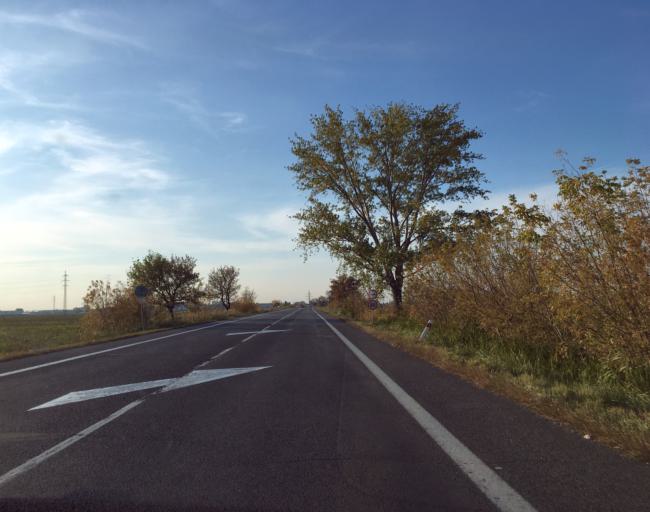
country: SK
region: Trnavsky
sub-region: Okres Galanta
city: Galanta
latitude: 48.1842
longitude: 17.7653
